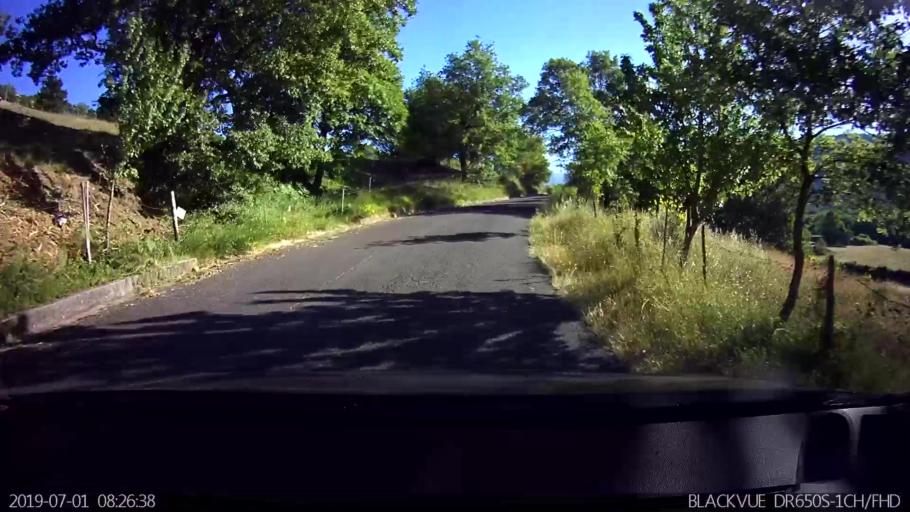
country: IT
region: Latium
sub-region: Provincia di Frosinone
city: Collepardo
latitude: 41.7698
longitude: 13.4042
